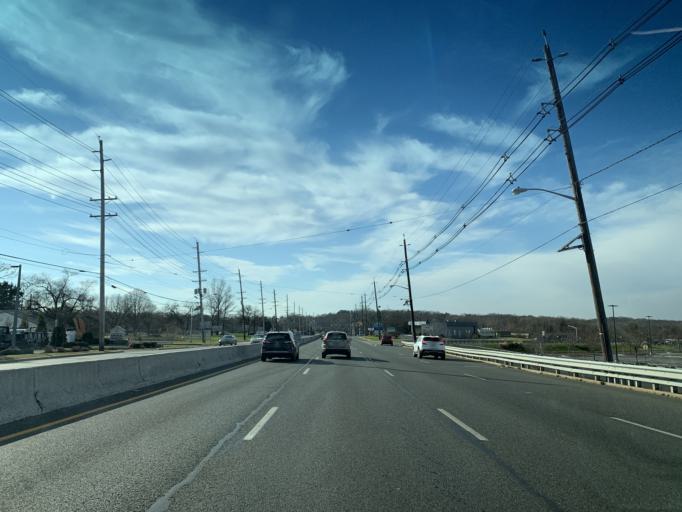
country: US
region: New Jersey
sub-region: Burlington County
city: Cinnaminson
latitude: 40.0064
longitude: -74.9758
